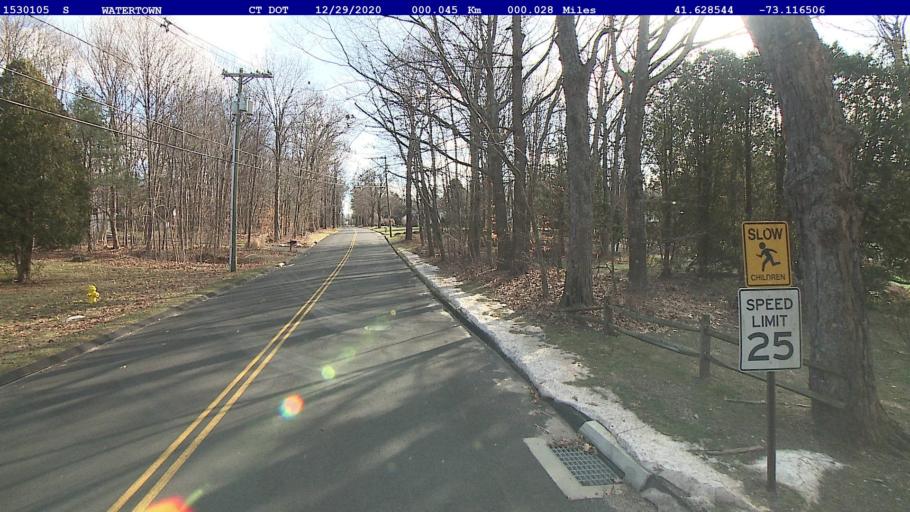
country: US
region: Connecticut
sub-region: Litchfield County
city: Watertown
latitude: 41.6285
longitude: -73.1165
